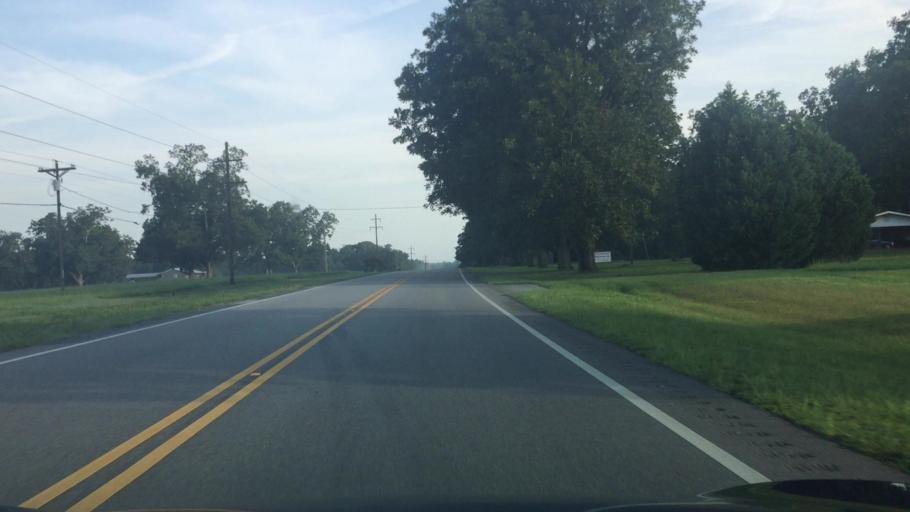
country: US
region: Alabama
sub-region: Covington County
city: Florala
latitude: 31.0487
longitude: -86.3867
